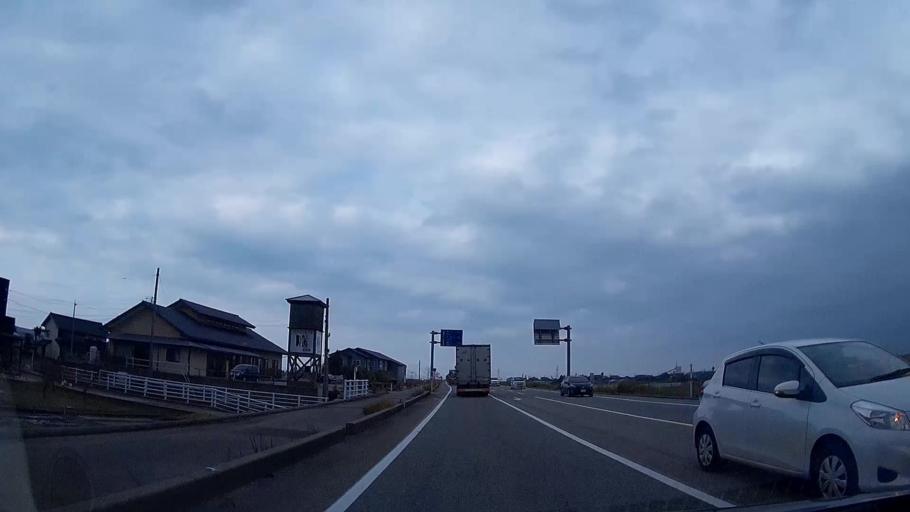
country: JP
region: Toyama
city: Nyuzen
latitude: 36.8923
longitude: 137.4443
